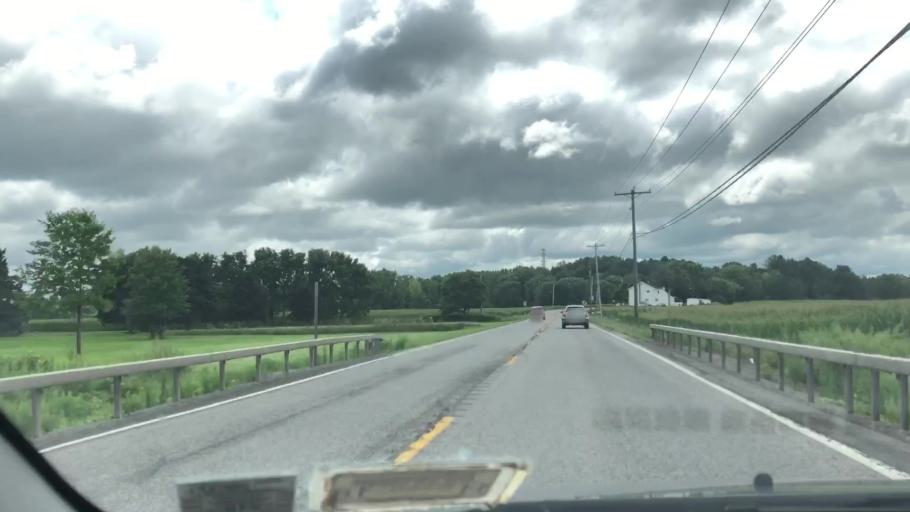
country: US
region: New York
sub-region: Wayne County
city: Macedon
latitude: 43.0998
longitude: -77.2940
